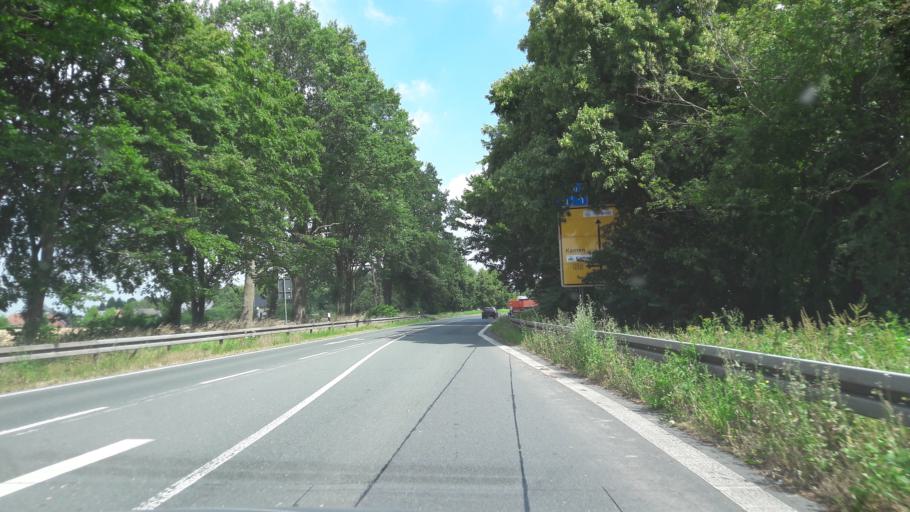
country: DE
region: North Rhine-Westphalia
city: Kamen
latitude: 51.5762
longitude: 7.6679
